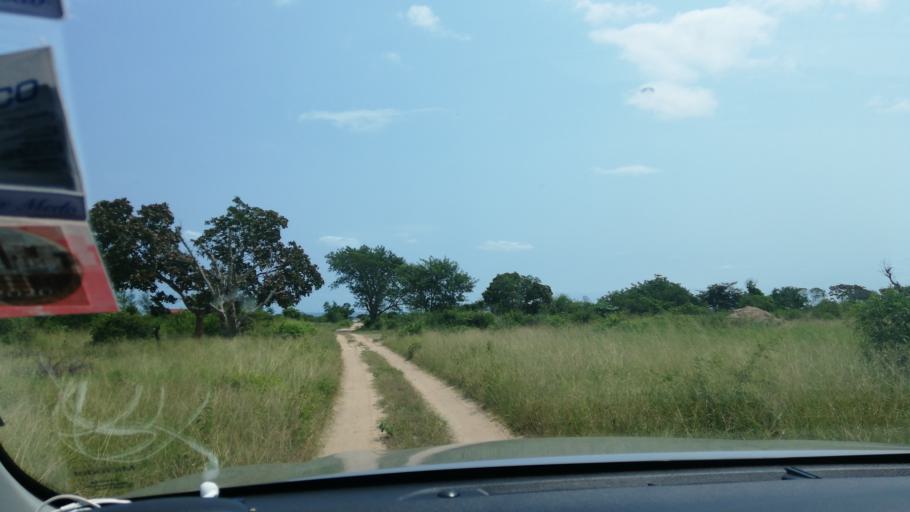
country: MZ
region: Maputo
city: Matola
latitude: -26.1101
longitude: 32.4150
